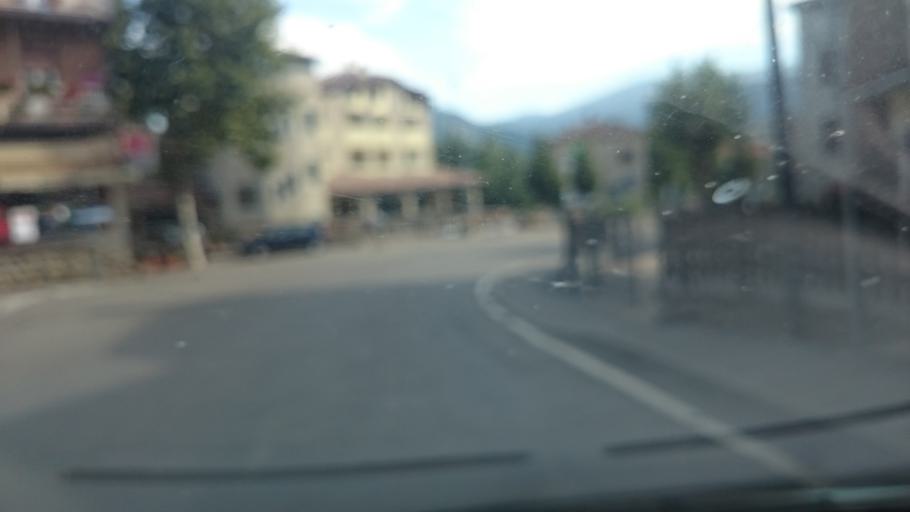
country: IT
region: Emilia-Romagna
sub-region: Provincia di Reggio Emilia
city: Villa Minozzo
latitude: 44.3644
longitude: 10.4668
